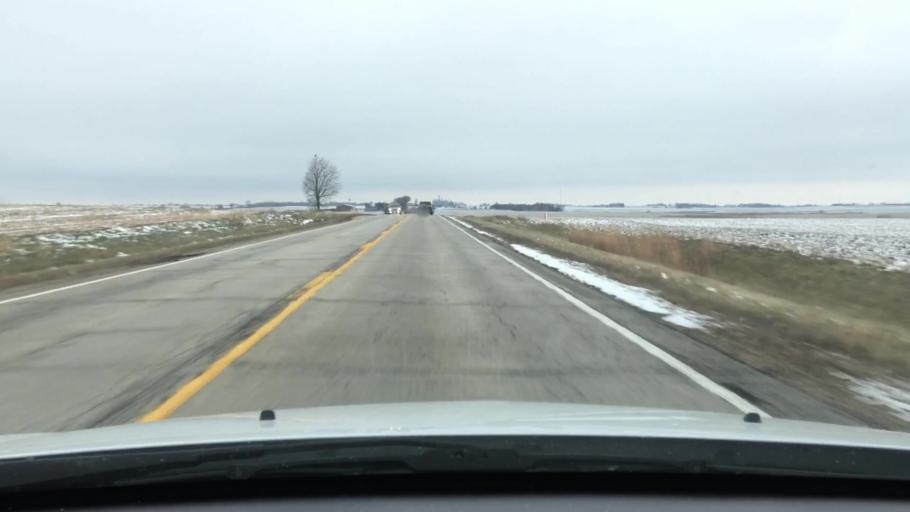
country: US
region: Illinois
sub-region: DeKalb County
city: Malta
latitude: 41.9357
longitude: -88.9099
